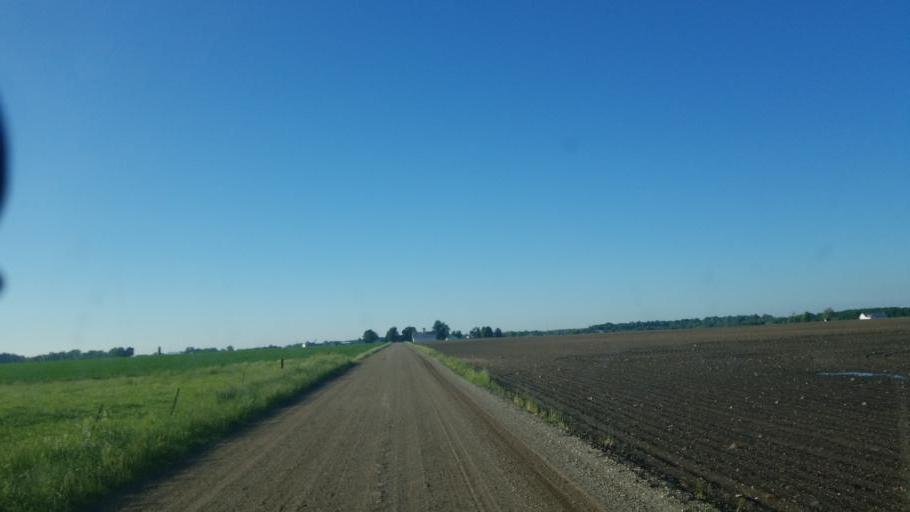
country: US
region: Indiana
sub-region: Marshall County
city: Bremen
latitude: 41.4187
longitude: -86.0975
